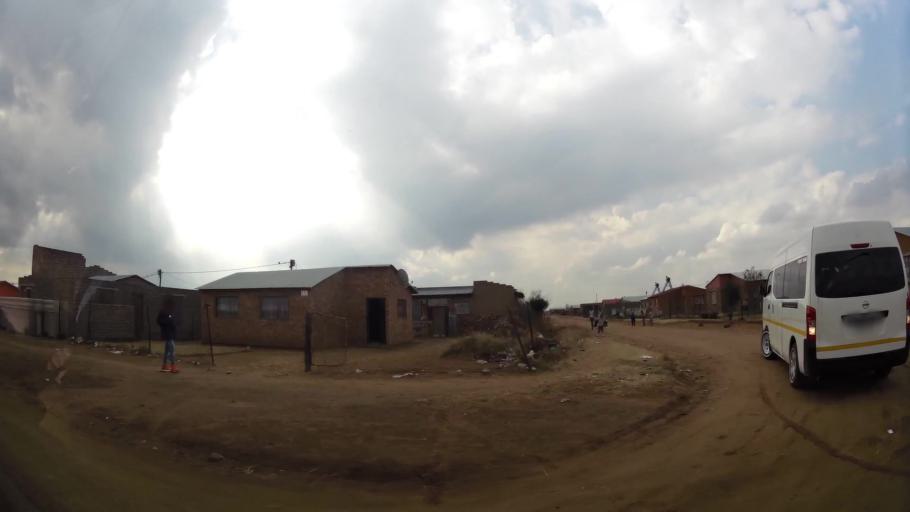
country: ZA
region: Orange Free State
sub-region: Fezile Dabi District Municipality
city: Sasolburg
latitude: -26.8524
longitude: 27.8941
